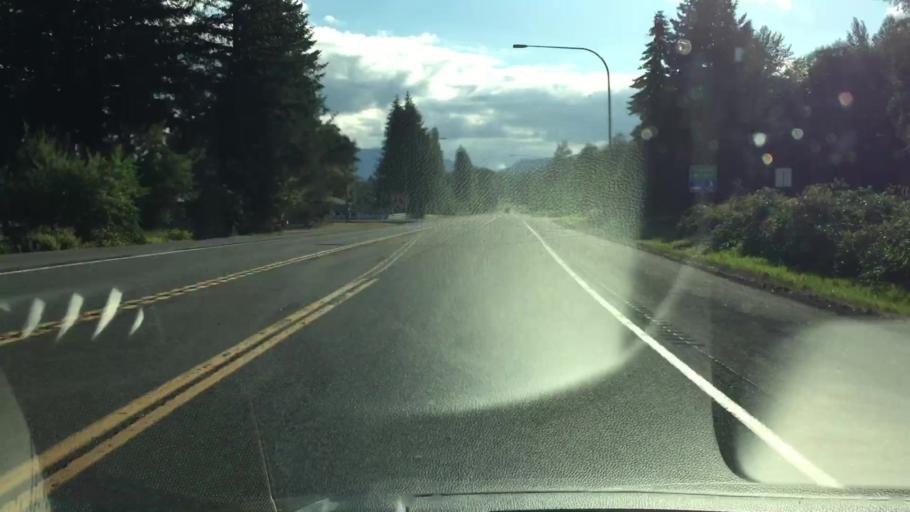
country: US
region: Washington
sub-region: Lewis County
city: Morton
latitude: 46.5198
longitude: -122.1542
